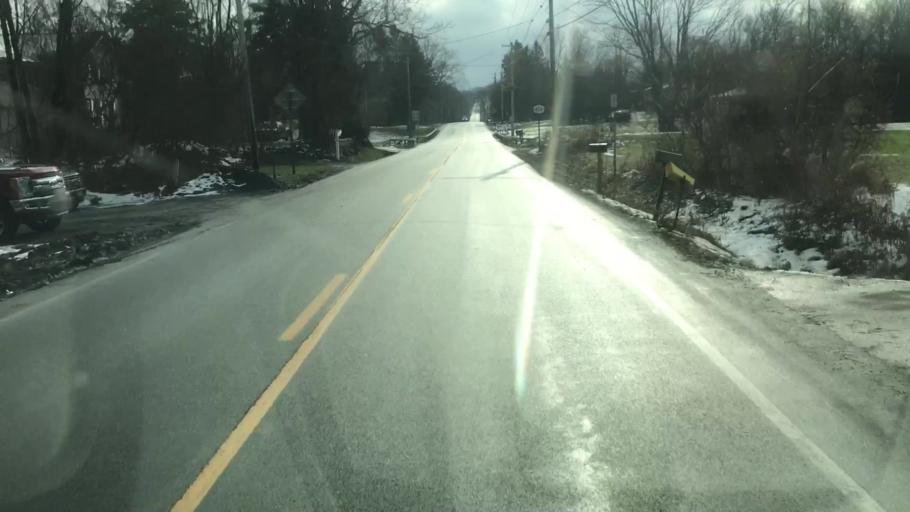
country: US
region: New York
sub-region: Onondaga County
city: Skaneateles
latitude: 42.8643
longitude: -76.4023
